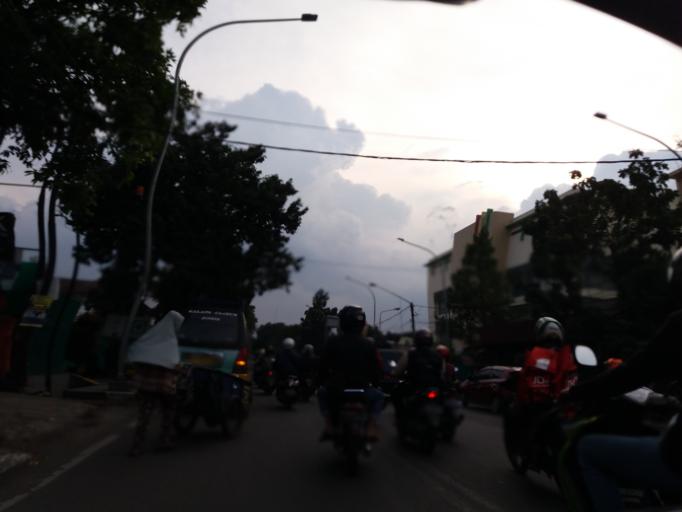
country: ID
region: West Java
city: Bandung
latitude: -6.9140
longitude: 107.6419
